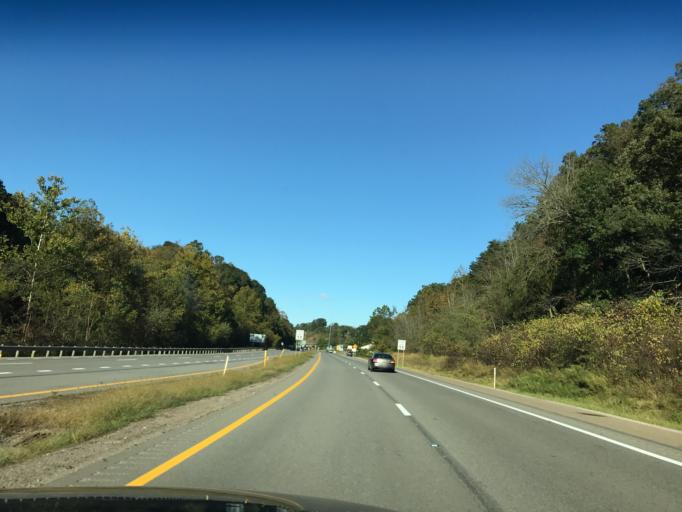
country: US
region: West Virginia
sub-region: Wood County
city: Parkersburg
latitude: 39.2667
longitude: -81.4906
